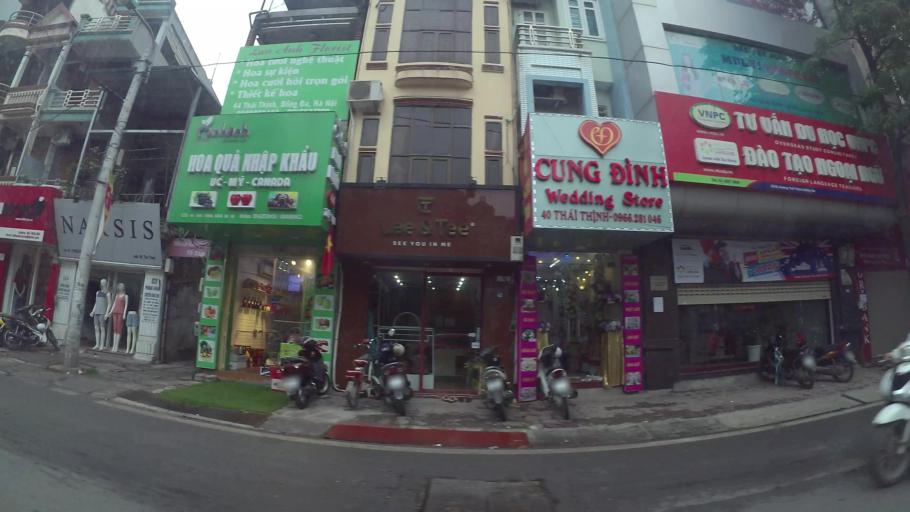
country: VN
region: Ha Noi
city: Dong Da
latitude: 21.0065
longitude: 105.8218
